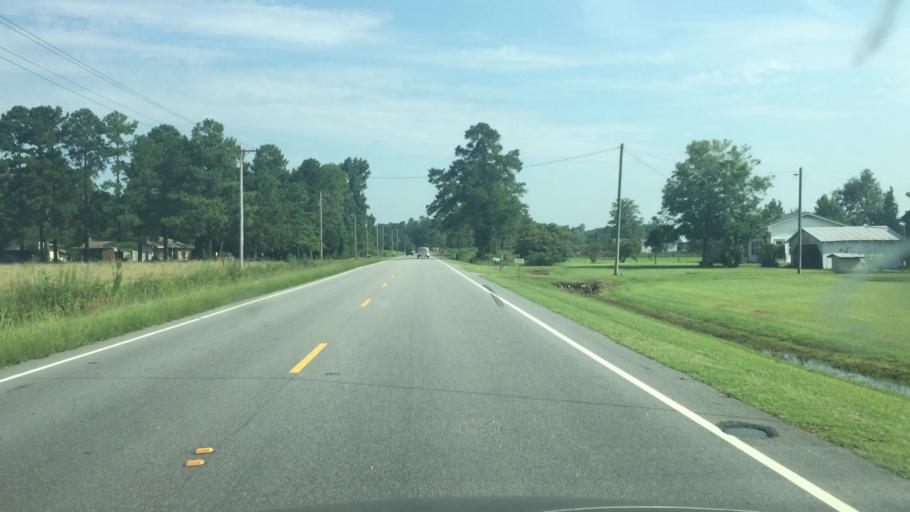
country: US
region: North Carolina
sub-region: Columbus County
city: Chadbourn
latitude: 34.2276
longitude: -78.8243
